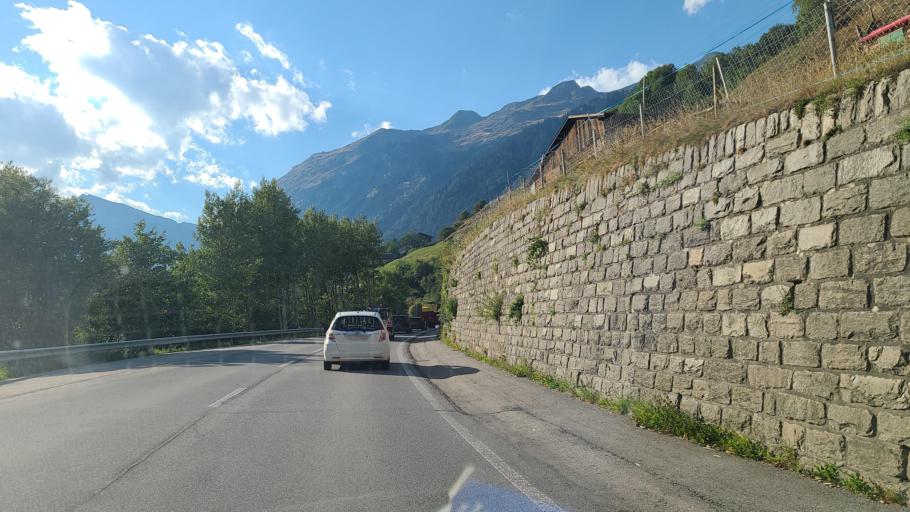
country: CH
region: Ticino
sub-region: Leventina District
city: Airolo
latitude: 46.5222
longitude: 8.6357
